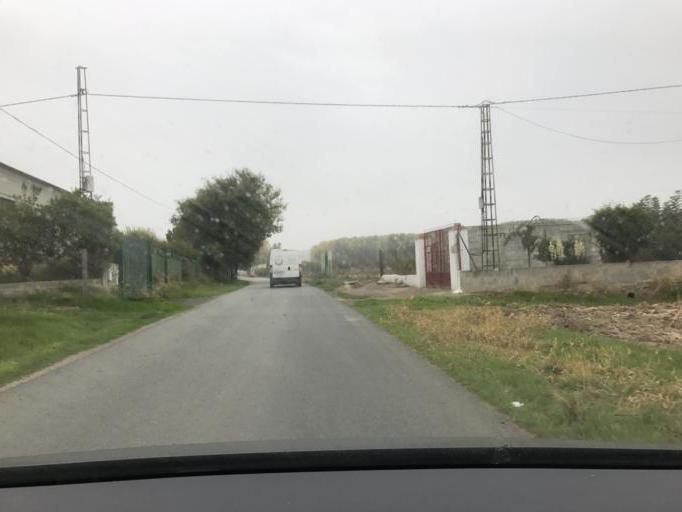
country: ES
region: Andalusia
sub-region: Provincia de Granada
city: Chauchina
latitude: 37.1787
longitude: -3.7275
